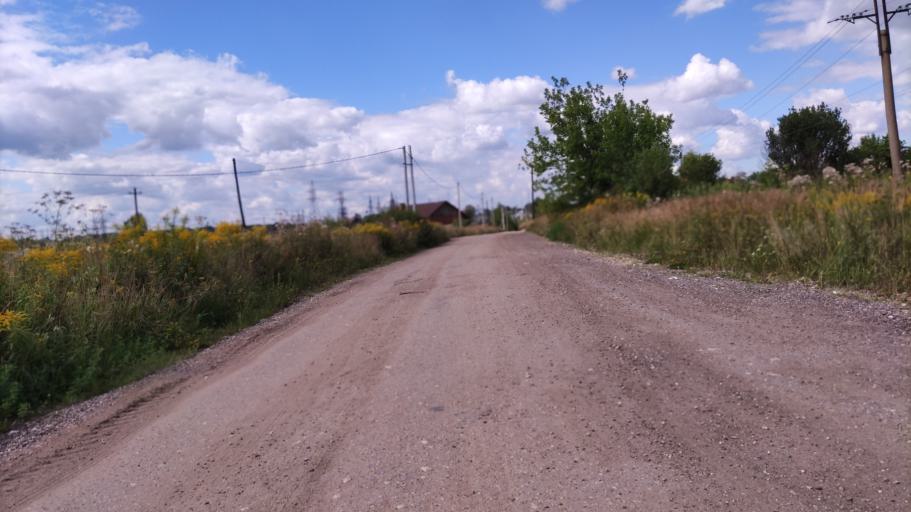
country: RU
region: Tverskaya
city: Rzhev
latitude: 56.2370
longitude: 34.3269
